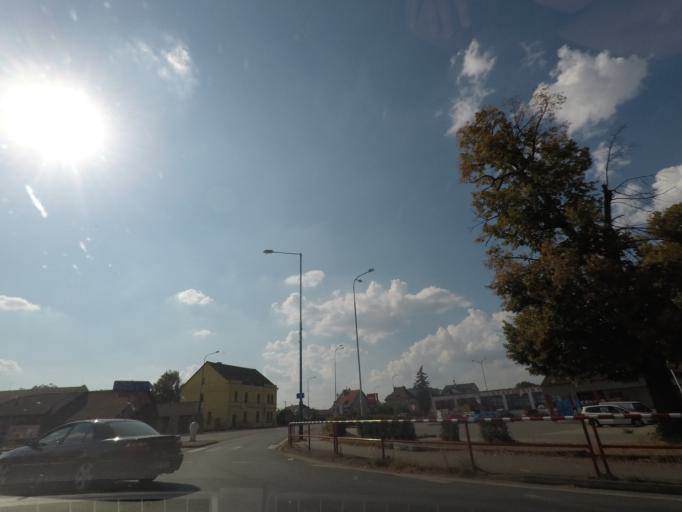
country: CZ
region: Kralovehradecky
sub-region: Okres Nachod
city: Jaromer
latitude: 50.3487
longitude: 15.9125
